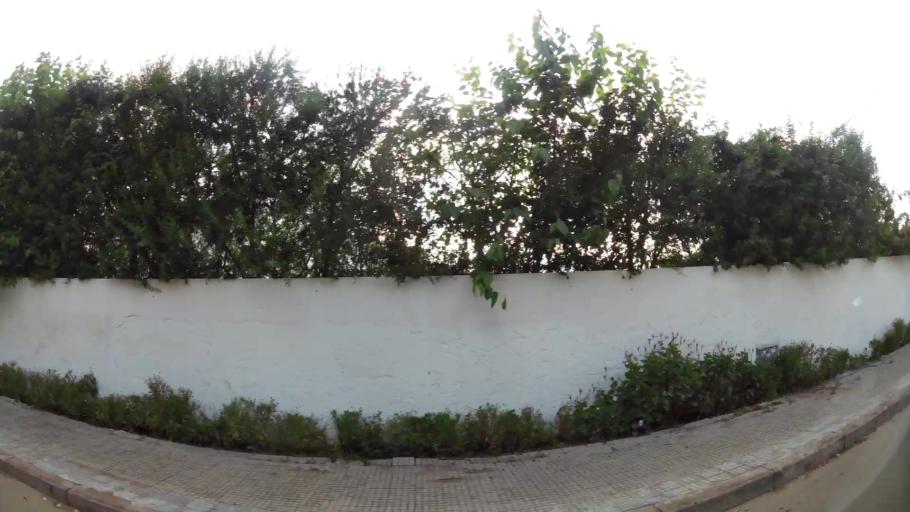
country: MA
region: Rabat-Sale-Zemmour-Zaer
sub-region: Rabat
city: Rabat
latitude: 33.9579
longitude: -6.8392
